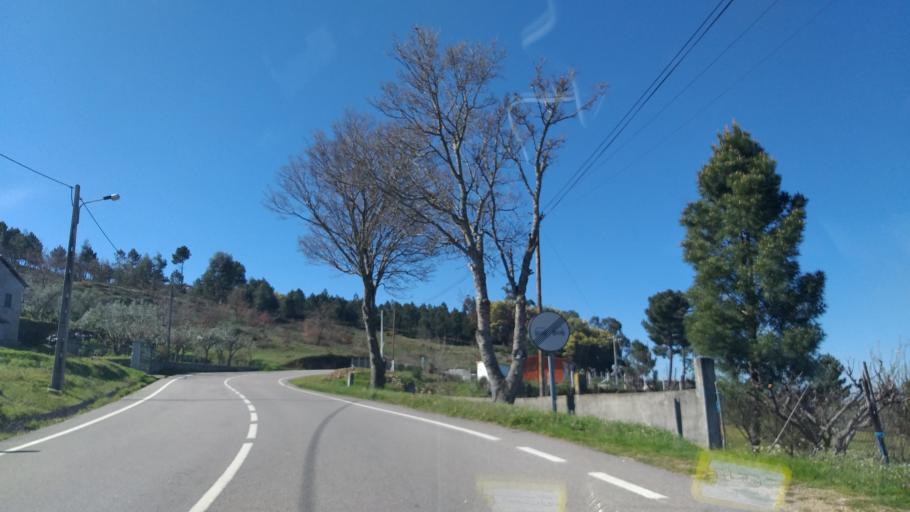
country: PT
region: Guarda
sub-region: Fornos de Algodres
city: Fornos de Algodres
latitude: 40.5160
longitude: -7.5599
